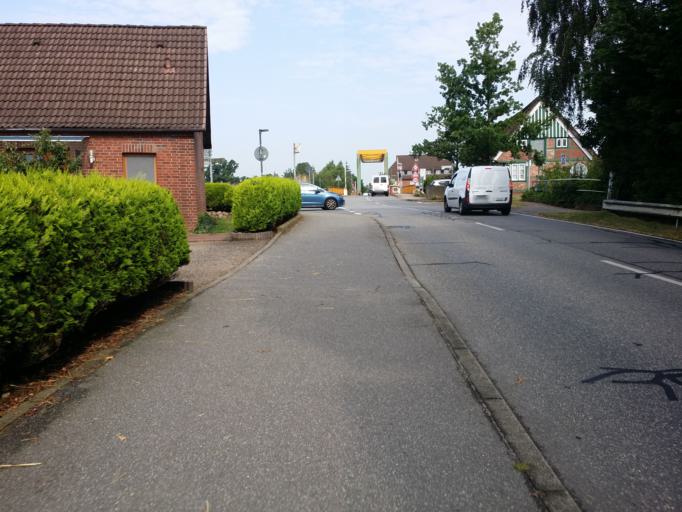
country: DE
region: Schleswig-Holstein
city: Heiligenstedten
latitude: 53.9286
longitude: 9.4704
